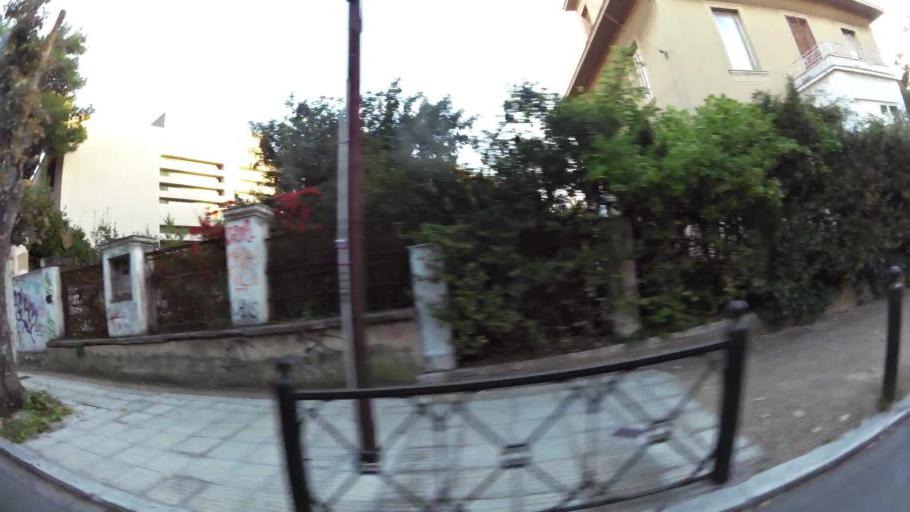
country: GR
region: Attica
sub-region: Nomarchia Athinas
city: Kifisia
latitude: 38.0754
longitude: 23.8181
